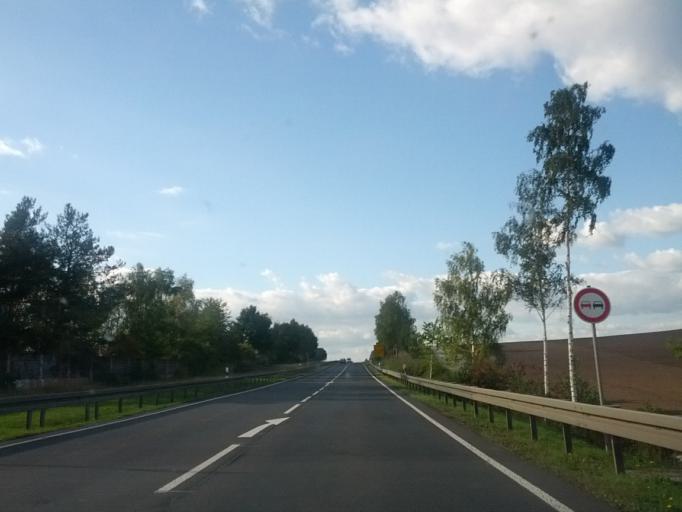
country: DE
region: Thuringia
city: Breitungen
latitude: 50.7668
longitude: 10.3369
